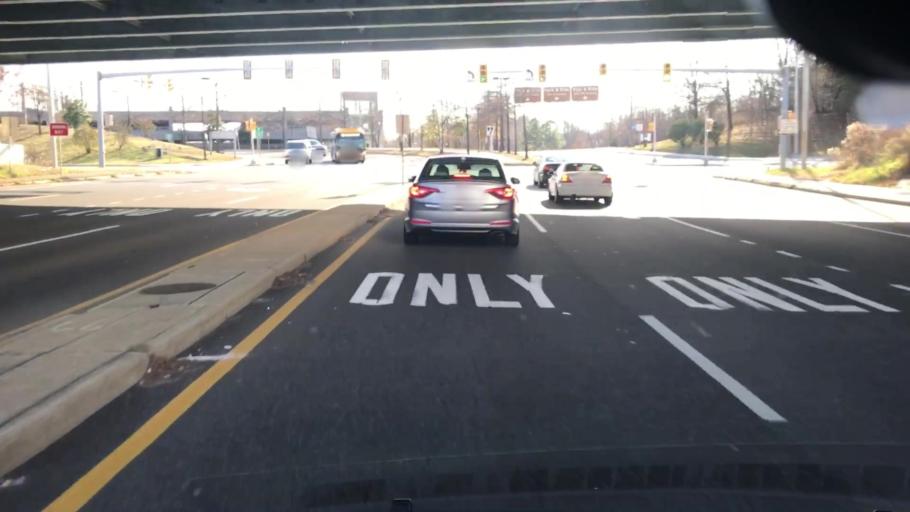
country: US
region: Virginia
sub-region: Fairfax County
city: Springfield
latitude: 38.7693
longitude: -77.1711
